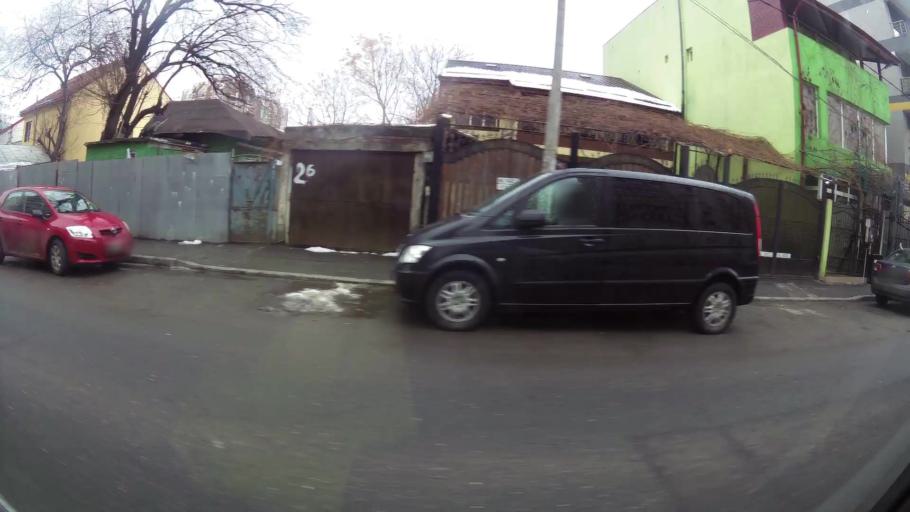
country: RO
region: Bucuresti
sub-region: Municipiul Bucuresti
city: Bucharest
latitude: 44.4189
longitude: 26.1296
